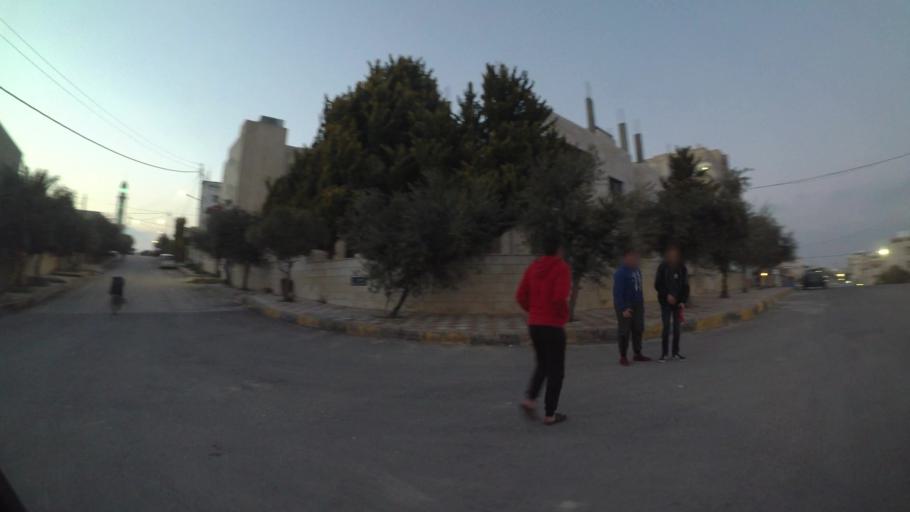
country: JO
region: Amman
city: Al Bunayyat ash Shamaliyah
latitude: 31.8865
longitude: 35.9230
